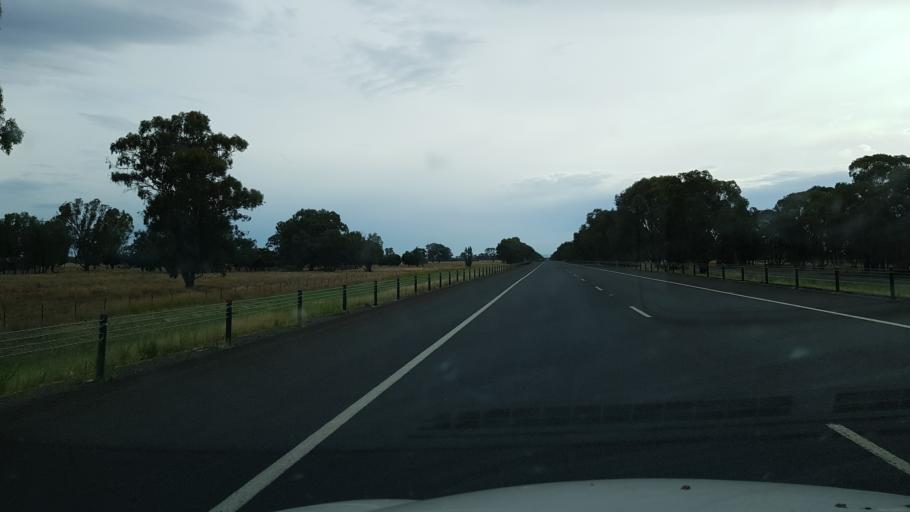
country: AU
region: Victoria
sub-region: Wangaratta
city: Wangaratta
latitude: -36.2805
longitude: 146.3996
